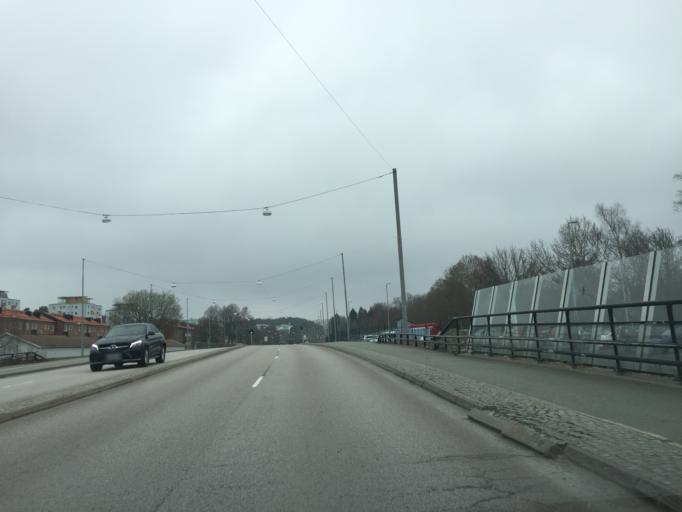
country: SE
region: Vaestra Goetaland
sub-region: Goteborg
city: Eriksbo
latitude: 57.7466
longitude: 12.0348
